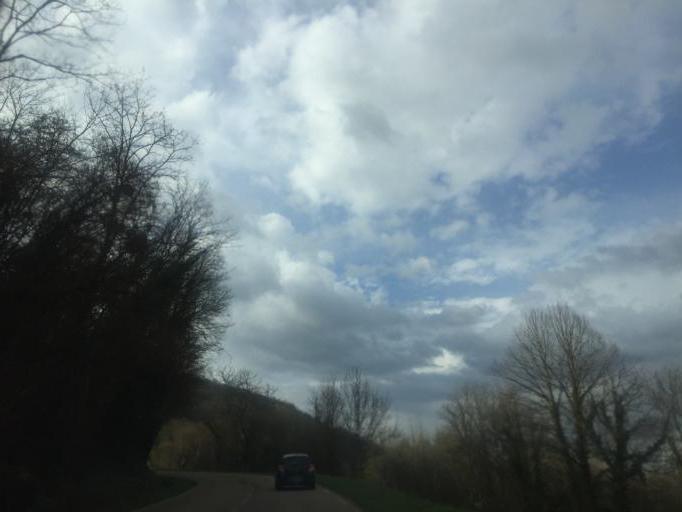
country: FR
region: Bourgogne
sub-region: Departement de l'Yonne
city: Avallon
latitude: 47.4632
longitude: 3.7584
